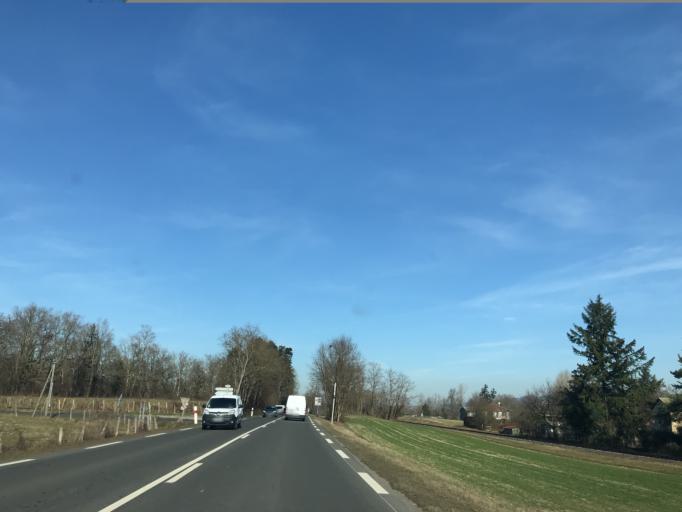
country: FR
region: Auvergne
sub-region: Departement du Puy-de-Dome
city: Peschadoires
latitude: 45.8046
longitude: 3.5161
